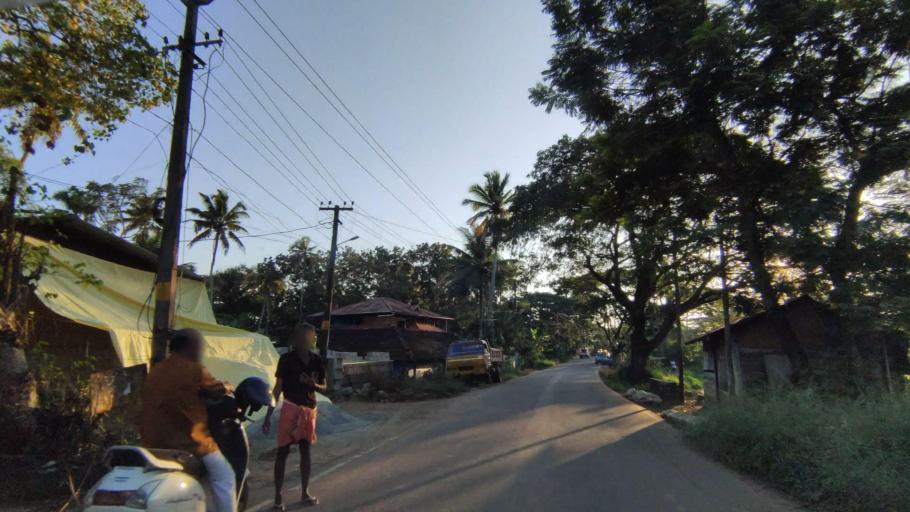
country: IN
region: Kerala
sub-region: Kottayam
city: Kottayam
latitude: 9.6254
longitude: 76.4886
